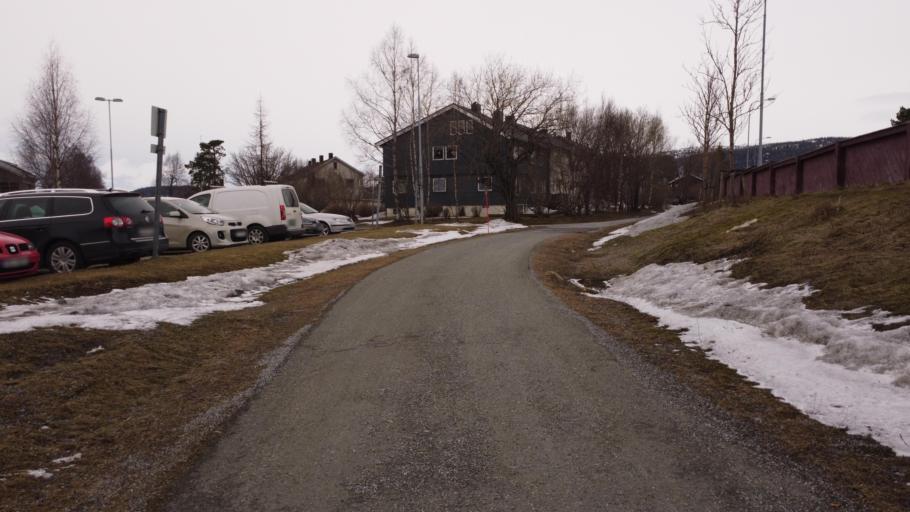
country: NO
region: Nordland
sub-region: Rana
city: Mo i Rana
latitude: 66.3111
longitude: 14.1538
